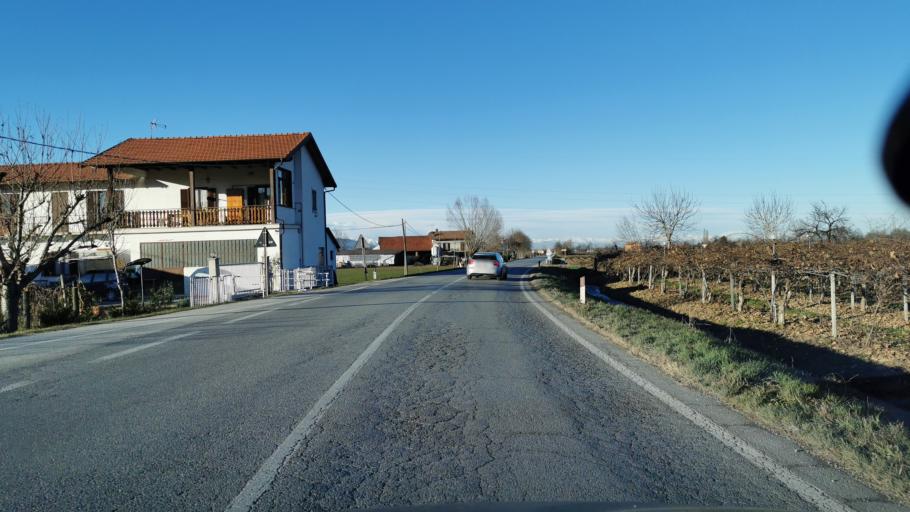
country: IT
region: Piedmont
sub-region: Provincia di Cuneo
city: Roata Rossi
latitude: 44.4285
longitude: 7.5449
